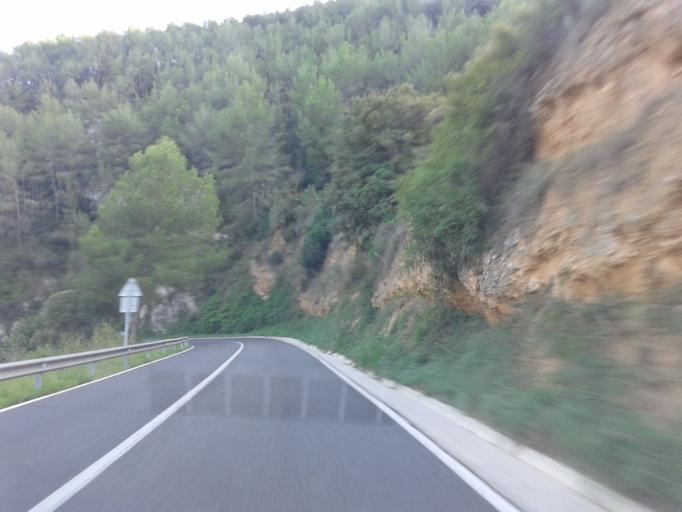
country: ES
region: Catalonia
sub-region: Provincia de Barcelona
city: Sant Pere de Ribes
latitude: 41.2730
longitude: 1.7642
